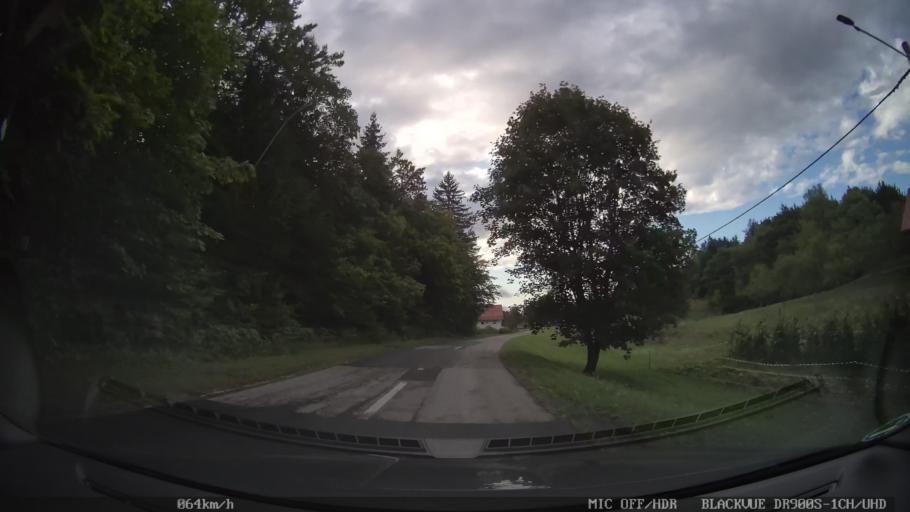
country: HR
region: Licko-Senjska
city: Jezerce
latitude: 44.9643
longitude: 15.5231
